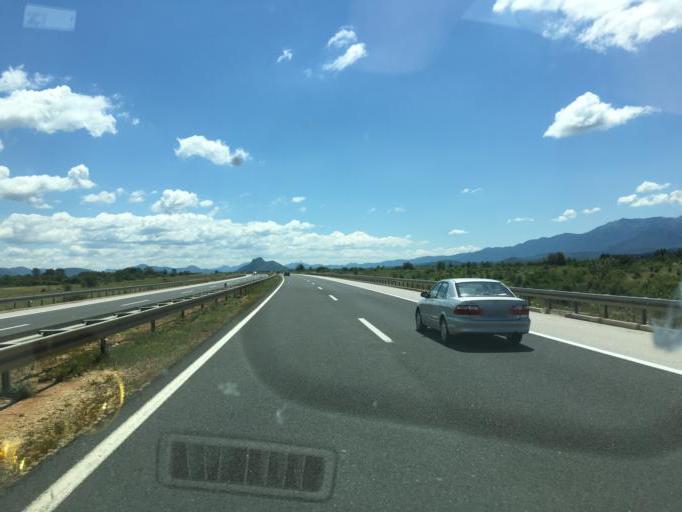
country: HR
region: Licko-Senjska
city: Gospic
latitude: 44.4924
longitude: 15.5395
